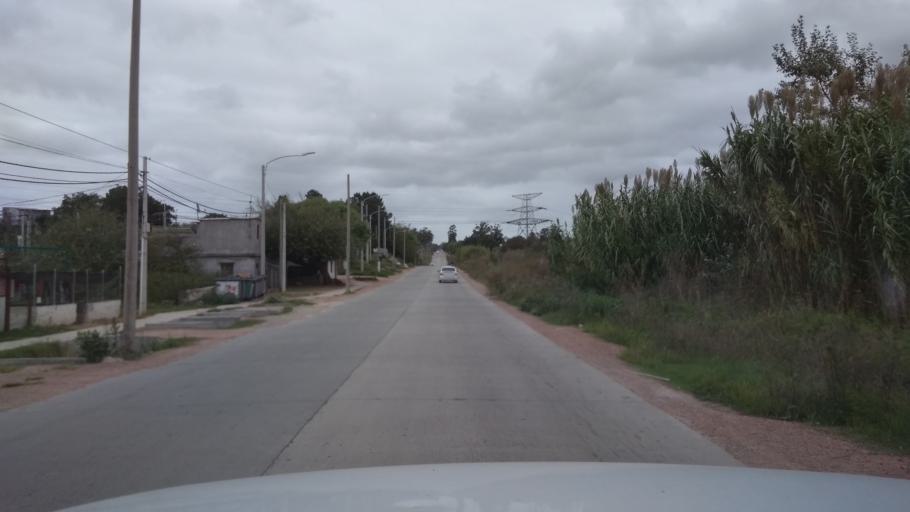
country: UY
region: Canelones
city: Toledo
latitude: -34.7901
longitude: -56.1455
